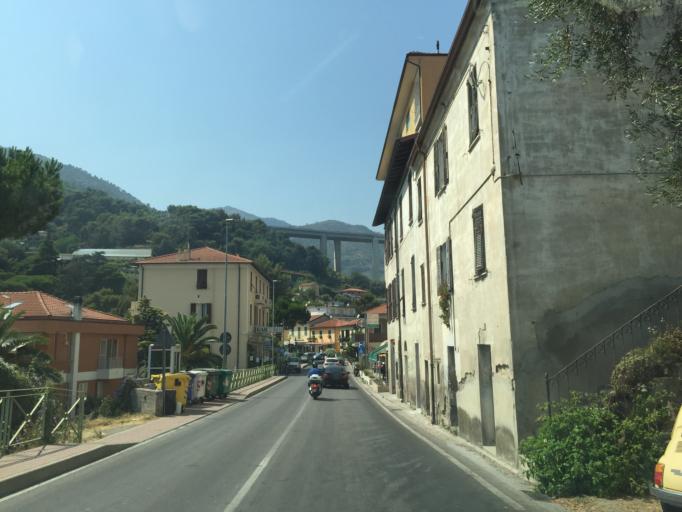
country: IT
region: Liguria
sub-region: Provincia di Imperia
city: Ventimiglia
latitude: 43.7940
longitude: 7.5649
